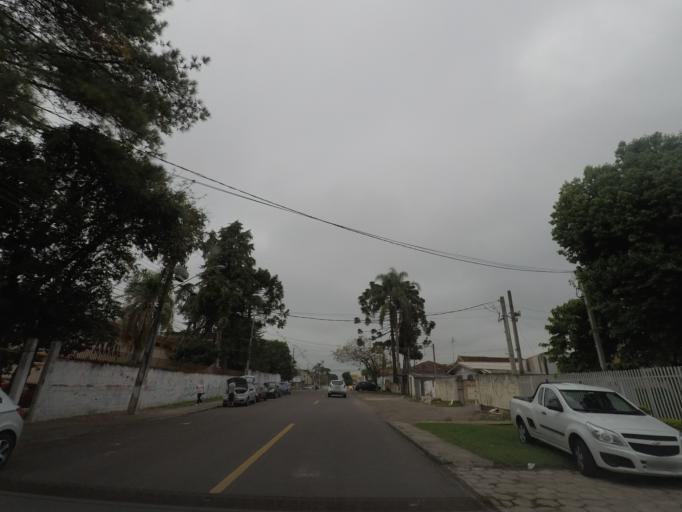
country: BR
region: Parana
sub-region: Sao Jose Dos Pinhais
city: Sao Jose dos Pinhais
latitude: -25.4995
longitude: -49.2359
